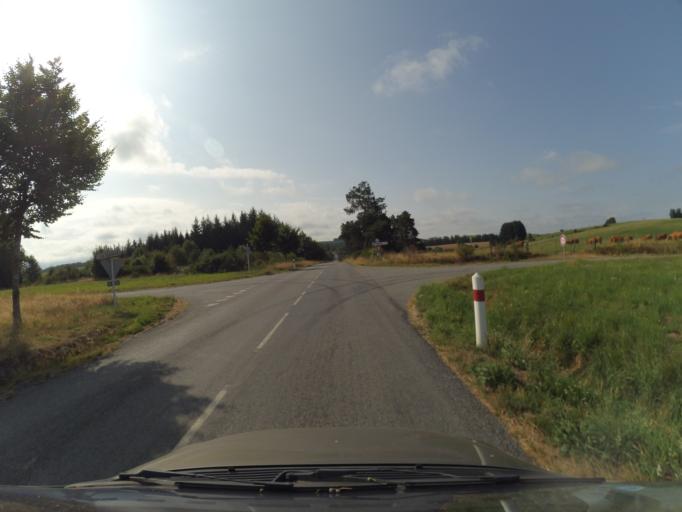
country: FR
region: Limousin
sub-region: Departement de la Correze
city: Meymac
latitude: 45.6267
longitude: 2.1037
